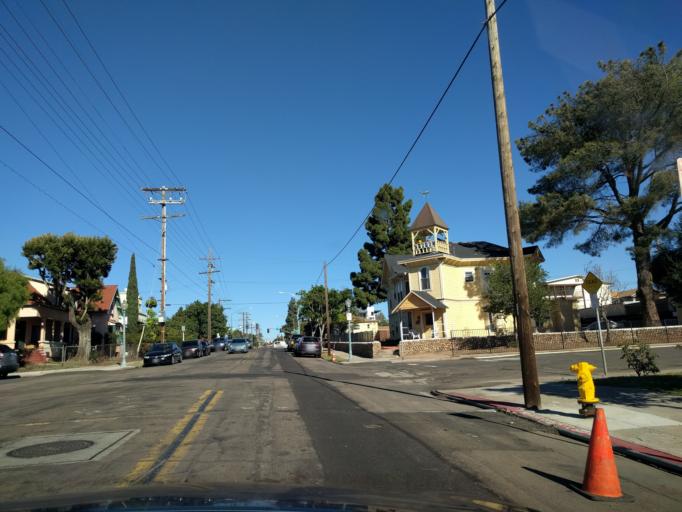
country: US
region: California
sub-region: San Diego County
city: San Diego
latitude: 32.7147
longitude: -117.1296
